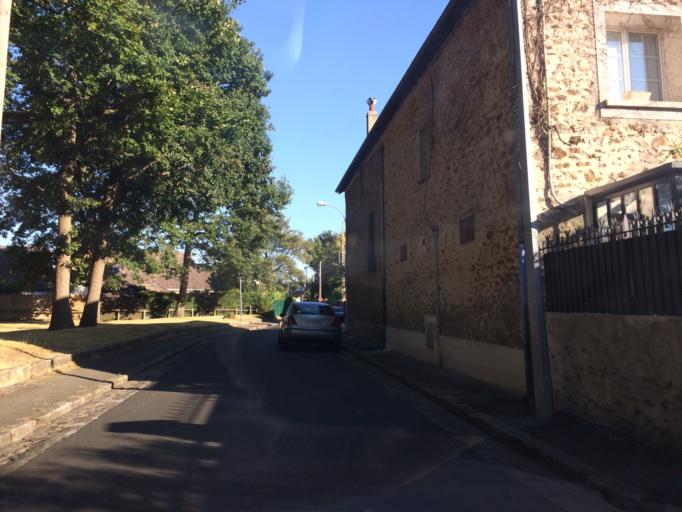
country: FR
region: Ile-de-France
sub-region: Departement de l'Essonne
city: Marolles-en-Hurepoix
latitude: 48.5646
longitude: 2.2976
